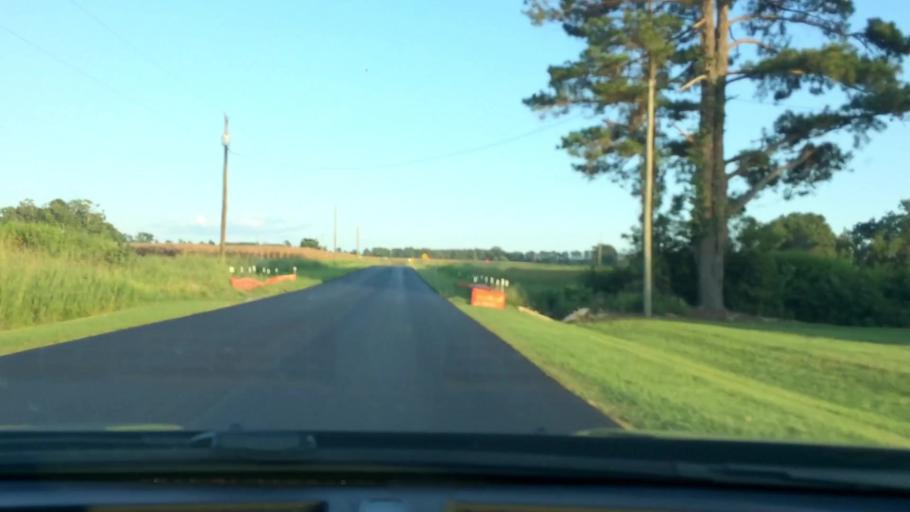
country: US
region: North Carolina
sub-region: Pitt County
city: Ayden
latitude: 35.4448
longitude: -77.4572
